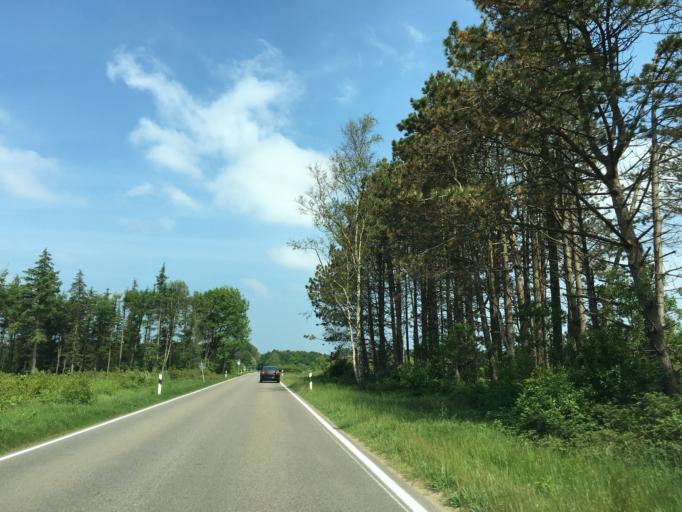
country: DE
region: Schleswig-Holstein
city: Norddorf
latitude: 54.6644
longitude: 8.3405
